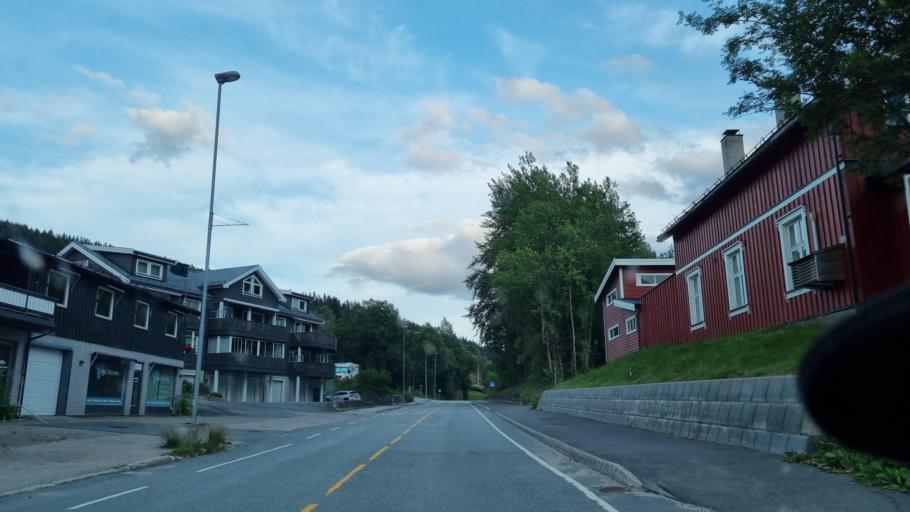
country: NO
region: Hedmark
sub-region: Trysil
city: Innbygda
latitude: 61.3118
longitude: 12.2692
